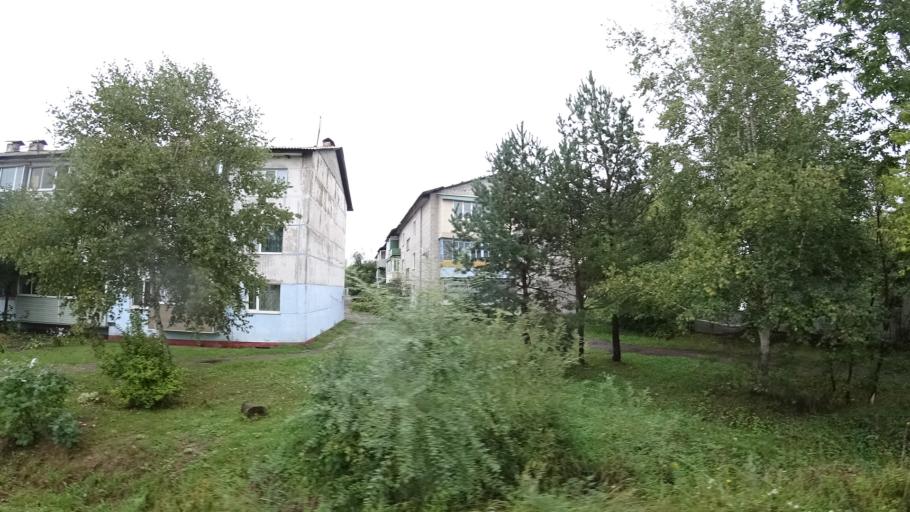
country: RU
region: Primorskiy
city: Monastyrishche
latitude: 44.1936
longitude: 132.4257
